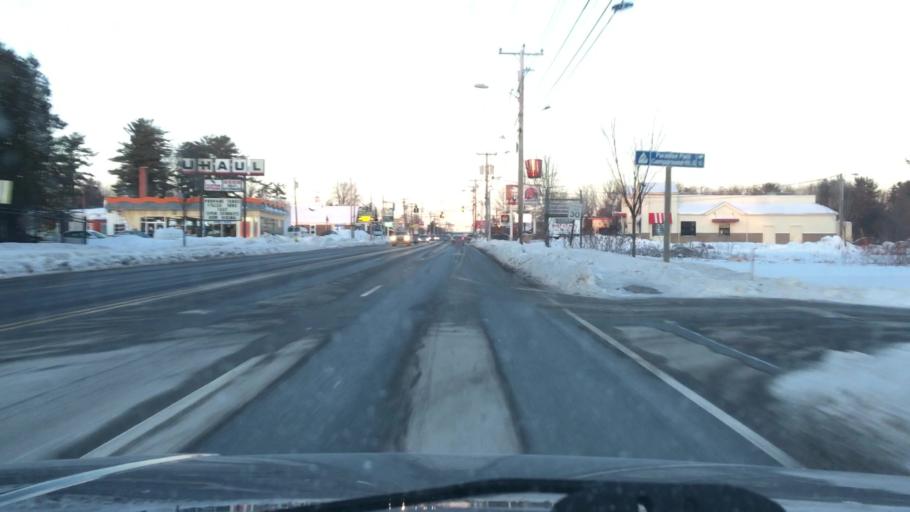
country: US
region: Maine
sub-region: York County
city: Saco
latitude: 43.5072
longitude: -70.4367
